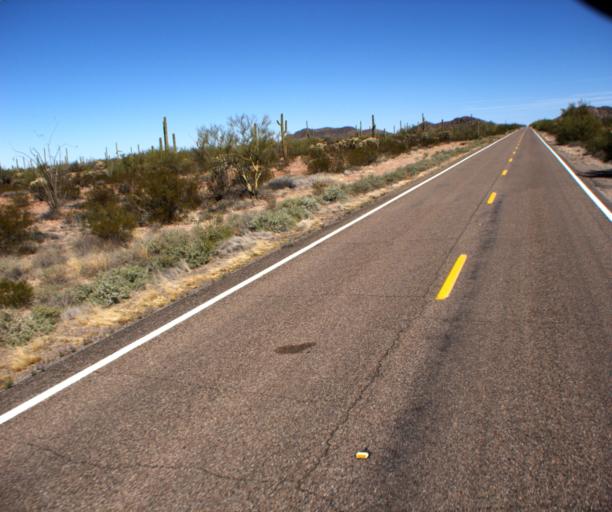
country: MX
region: Sonora
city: Sonoyta
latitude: 32.0600
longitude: -112.7874
